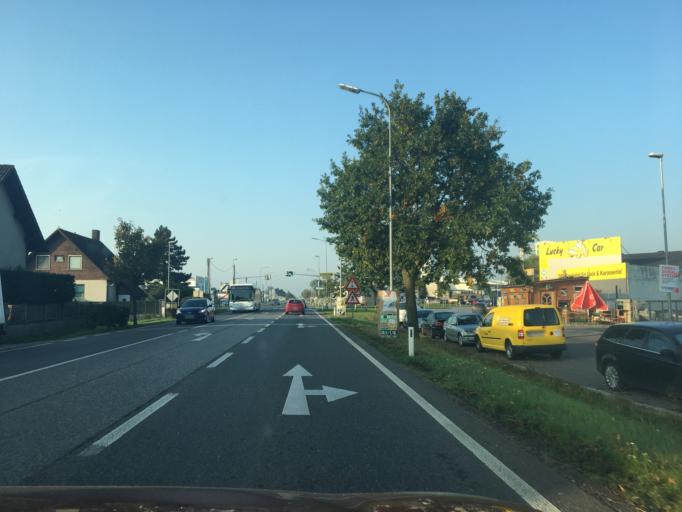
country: AT
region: Lower Austria
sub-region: Politischer Bezirk Mistelbach
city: Grossebersdorf
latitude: 48.3322
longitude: 16.4555
